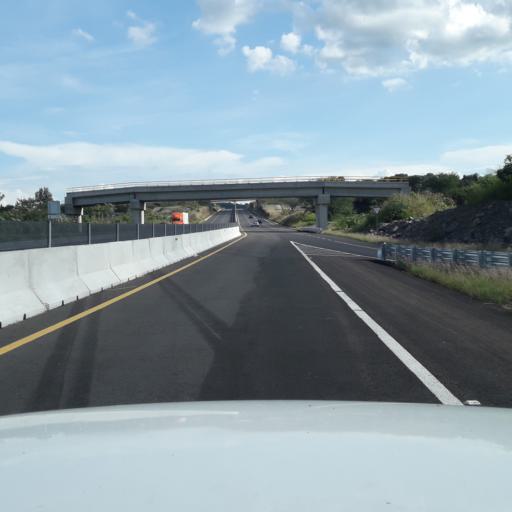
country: MX
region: Jalisco
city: Arenal
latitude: 20.7916
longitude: -103.7124
